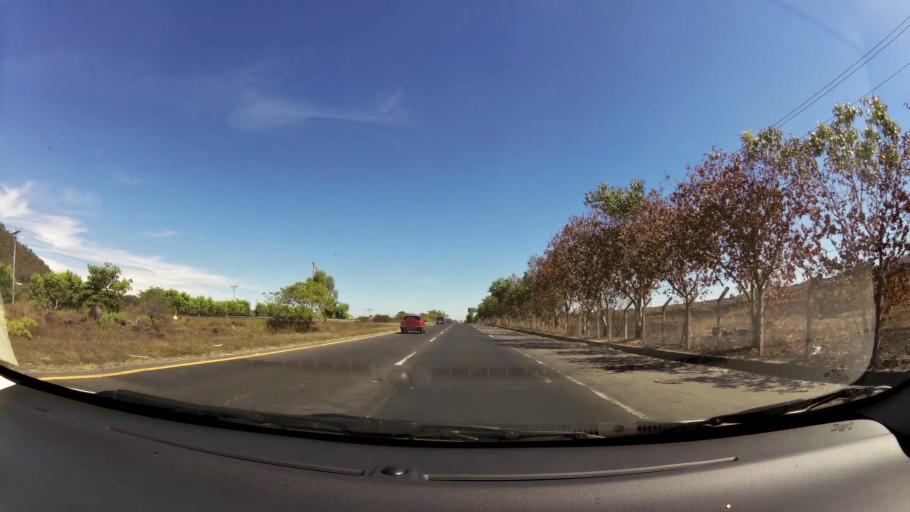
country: SV
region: La Libertad
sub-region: Distrito de Quezaltepeque
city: Quezaltepeque
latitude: 13.8041
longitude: -89.3299
